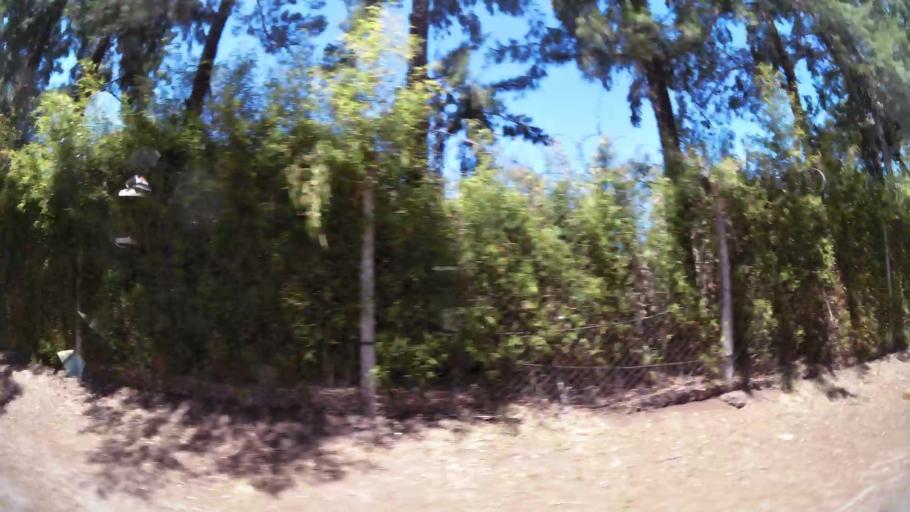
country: AR
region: Buenos Aires
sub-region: Partido de Tigre
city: Tigre
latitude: -34.4432
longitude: -58.5409
